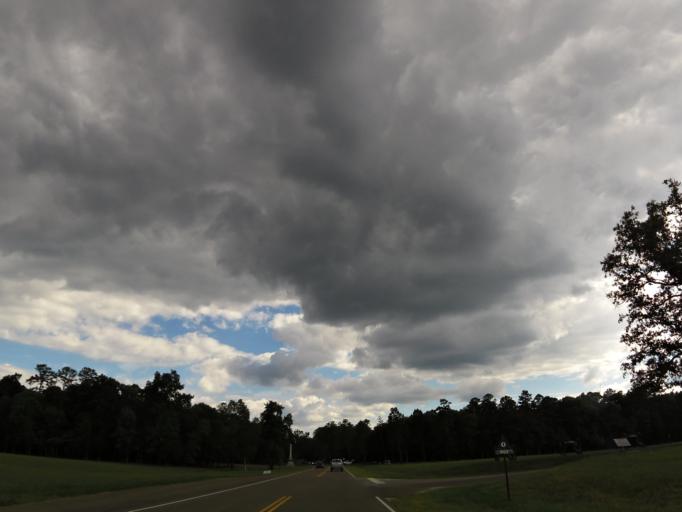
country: US
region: Georgia
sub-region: Catoosa County
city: Fort Oglethorpe
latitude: 34.9382
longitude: -85.2592
